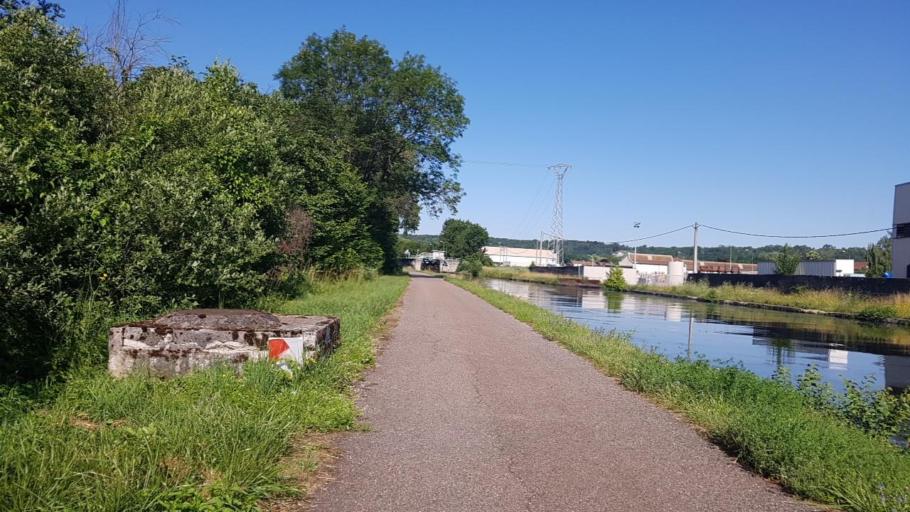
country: FR
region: Lorraine
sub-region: Departement de Meurthe-et-Moselle
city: Foug
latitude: 48.6764
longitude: 5.8019
